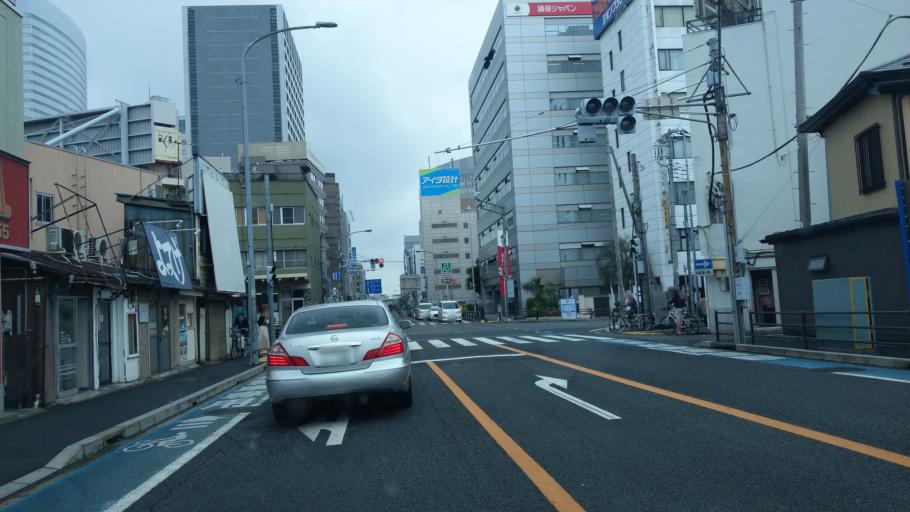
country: JP
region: Saitama
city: Yono
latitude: 35.9075
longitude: 139.6169
